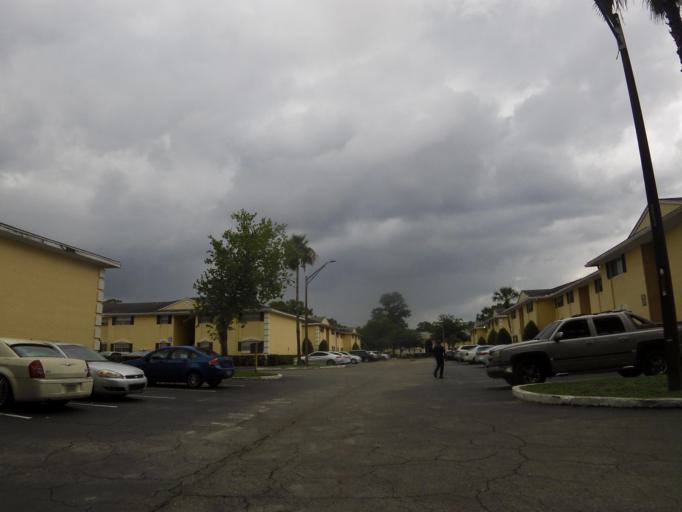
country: US
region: Florida
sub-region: Duval County
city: Jacksonville
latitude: 30.4050
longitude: -81.6625
